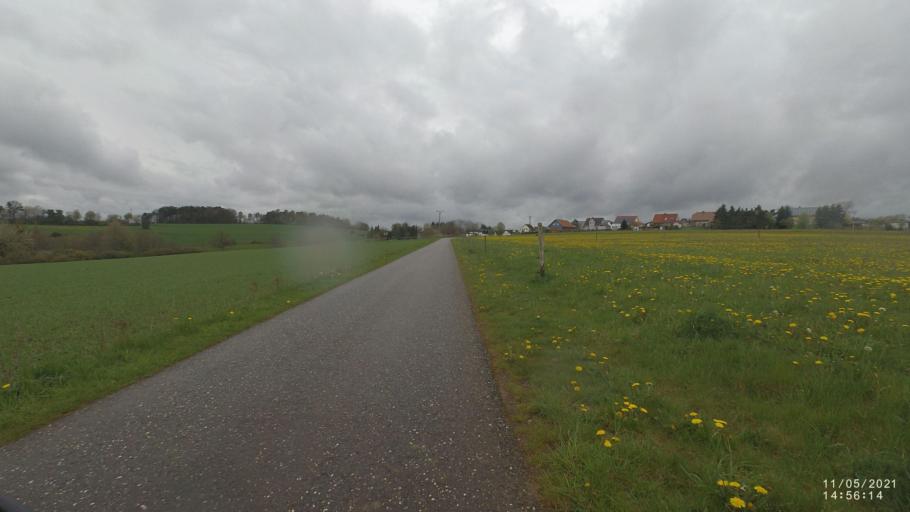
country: DE
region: Rheinland-Pfalz
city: Ditscheid
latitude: 50.2956
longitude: 7.0718
